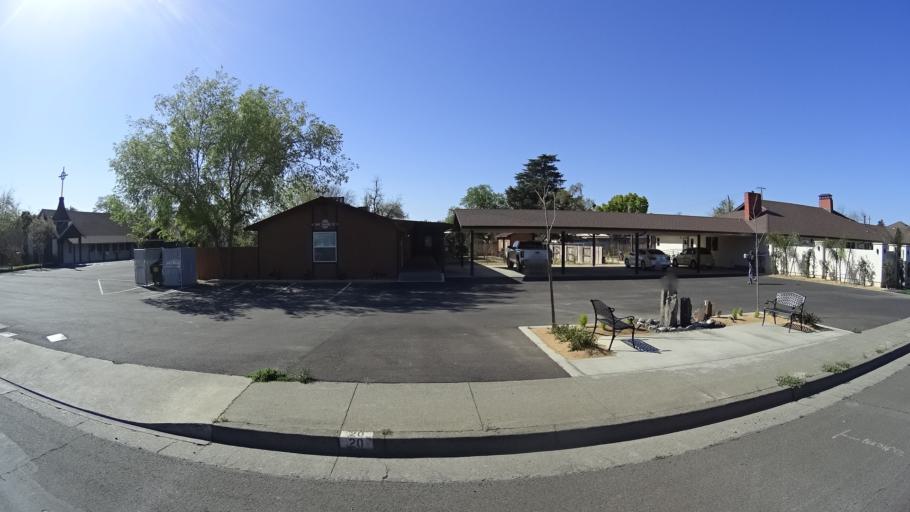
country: US
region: California
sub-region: Glenn County
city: Orland
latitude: 39.7473
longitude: -122.1867
